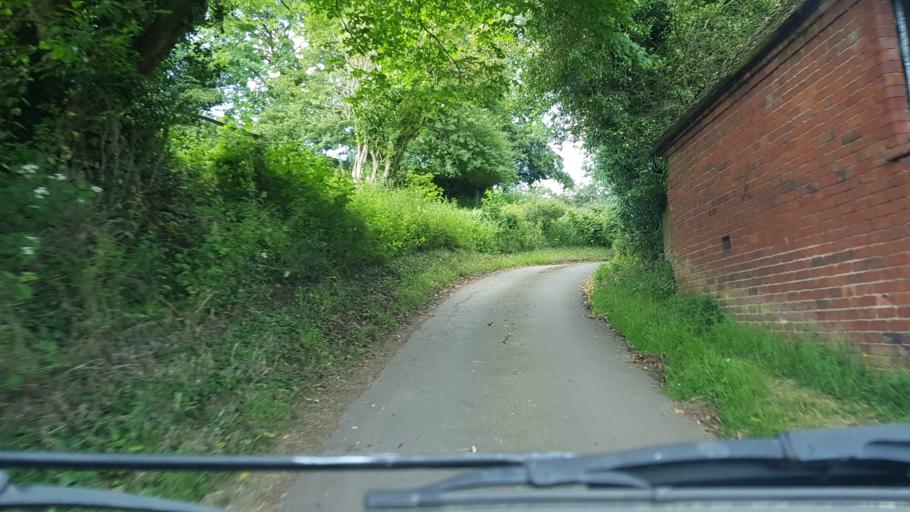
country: GB
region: England
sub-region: Shropshire
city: Romsley
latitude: 52.4630
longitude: -2.2658
